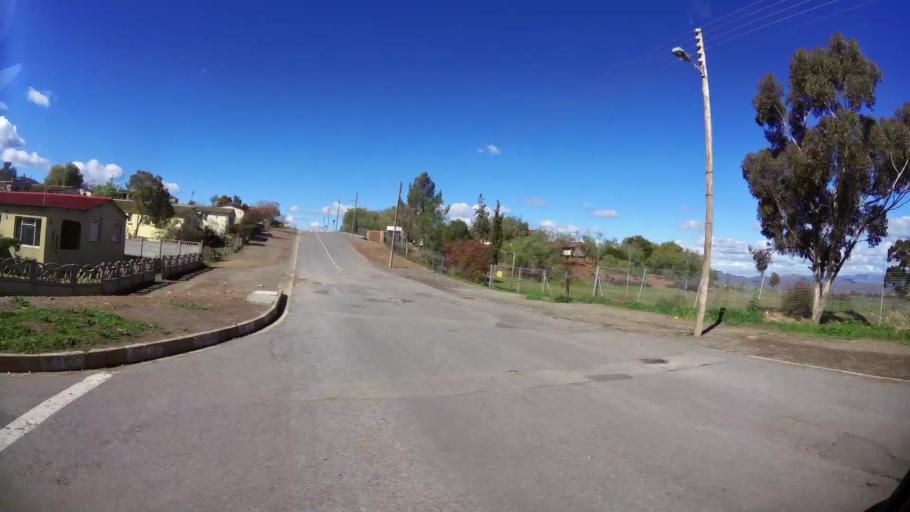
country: ZA
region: Western Cape
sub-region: Cape Winelands District Municipality
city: Ashton
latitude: -33.7923
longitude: 19.8977
